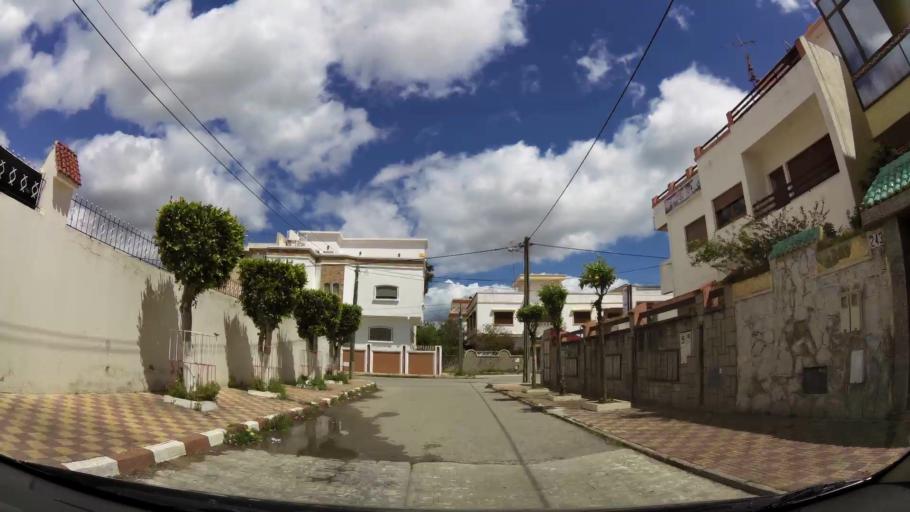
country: MA
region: Tanger-Tetouan
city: Tetouan
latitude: 35.5823
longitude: -5.3478
